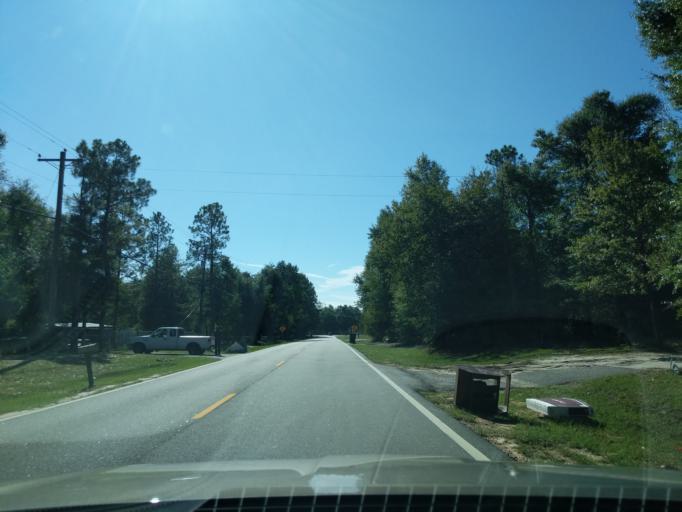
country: US
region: Georgia
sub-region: Richmond County
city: Hephzibah
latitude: 33.2594
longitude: -82.0077
